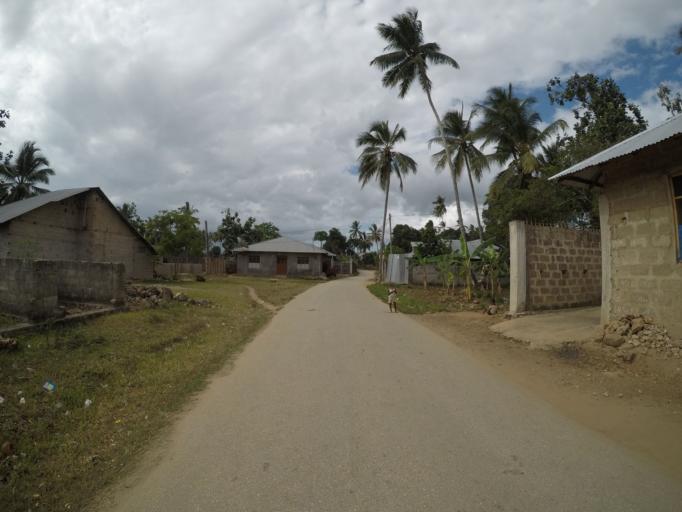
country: TZ
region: Zanzibar Central/South
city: Koani
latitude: -6.1943
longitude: 39.2642
